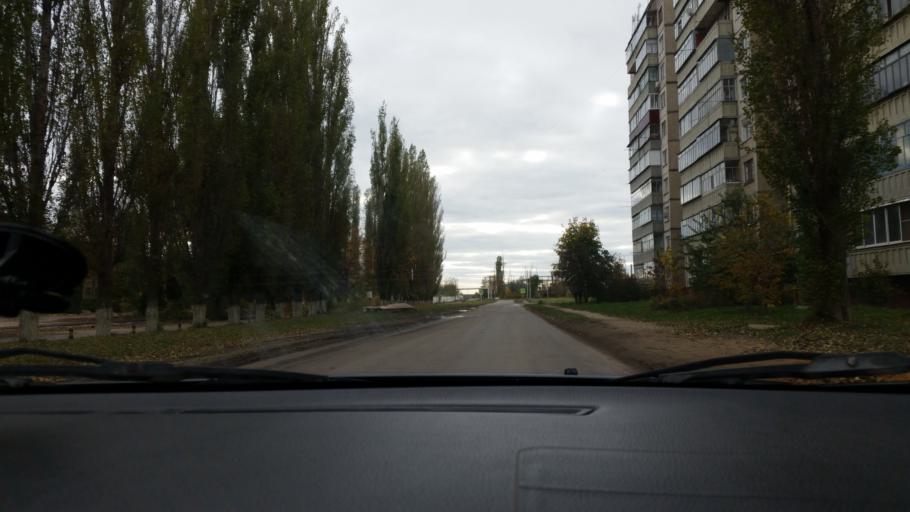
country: RU
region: Lipetsk
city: Gryazi
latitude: 52.4739
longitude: 39.9464
